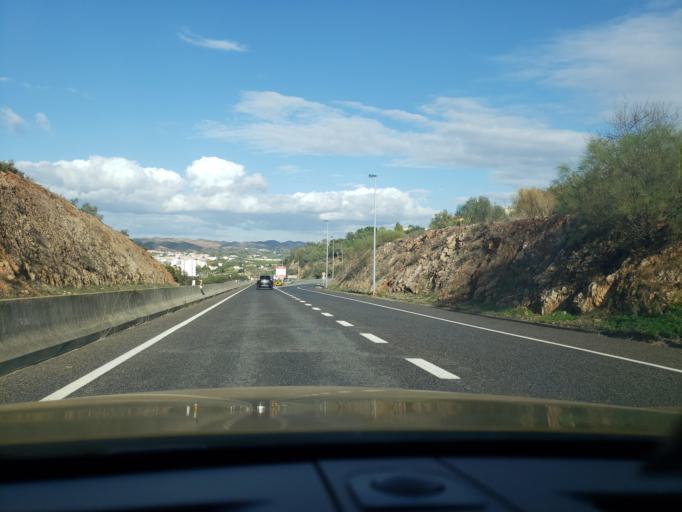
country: PT
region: Faro
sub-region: Silves
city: Silves
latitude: 37.1813
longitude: -8.4409
